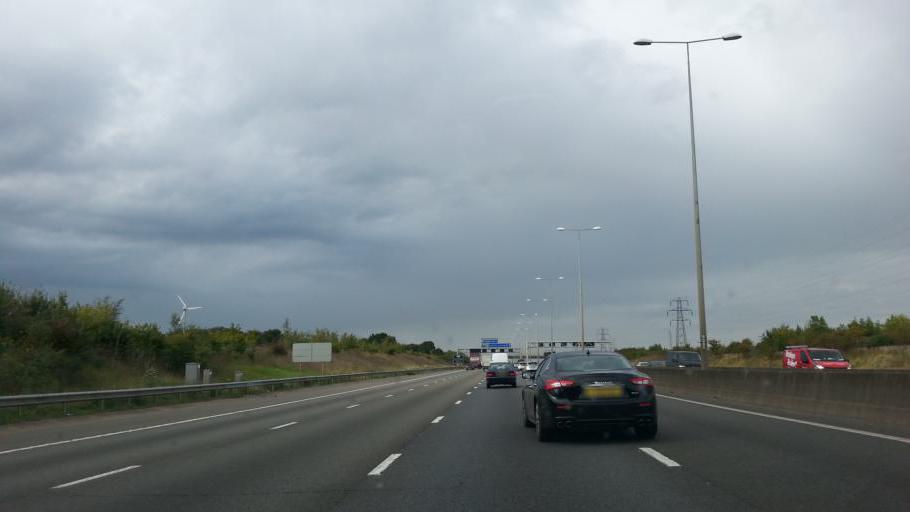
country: GB
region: England
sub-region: Hertfordshire
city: Redbourn
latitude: 51.7977
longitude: -0.4129
